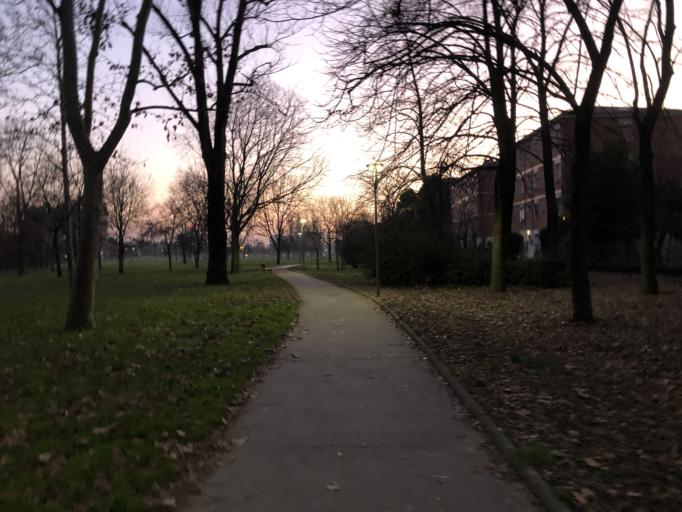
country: IT
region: Emilia-Romagna
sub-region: Provincia di Modena
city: Modena
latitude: 44.6461
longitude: 10.9044
